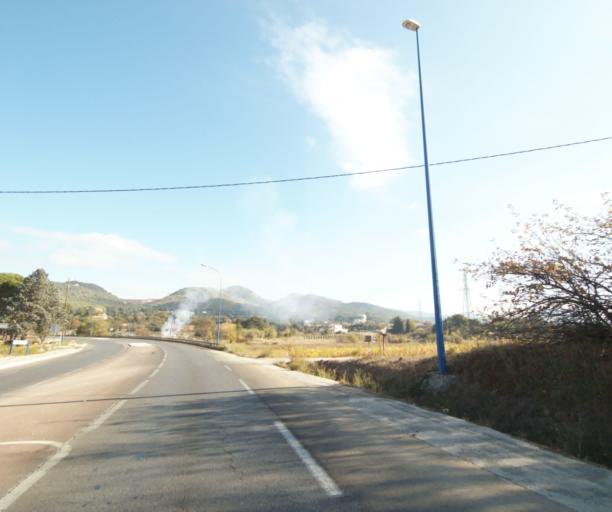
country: FR
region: Provence-Alpes-Cote d'Azur
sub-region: Departement des Bouches-du-Rhone
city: Allauch
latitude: 43.3239
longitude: 5.4805
